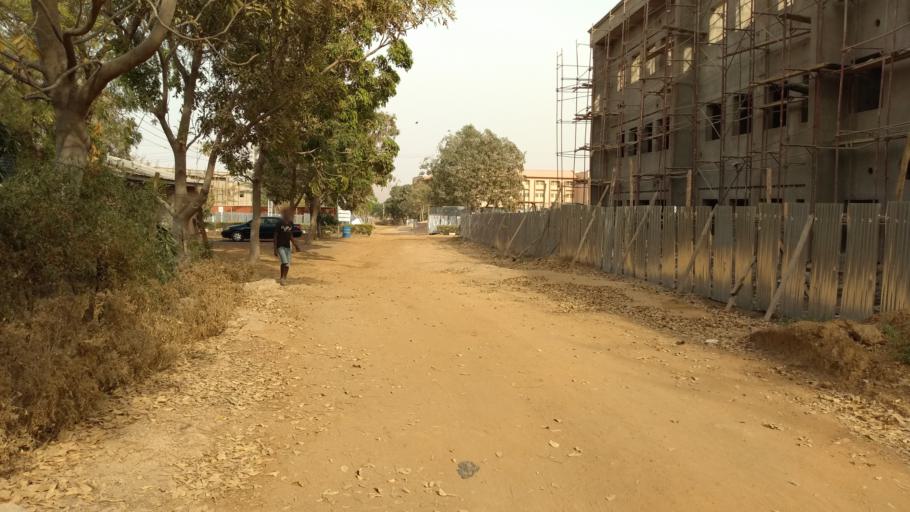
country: NG
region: Gombe
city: Gombe
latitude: 10.3077
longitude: 11.1745
